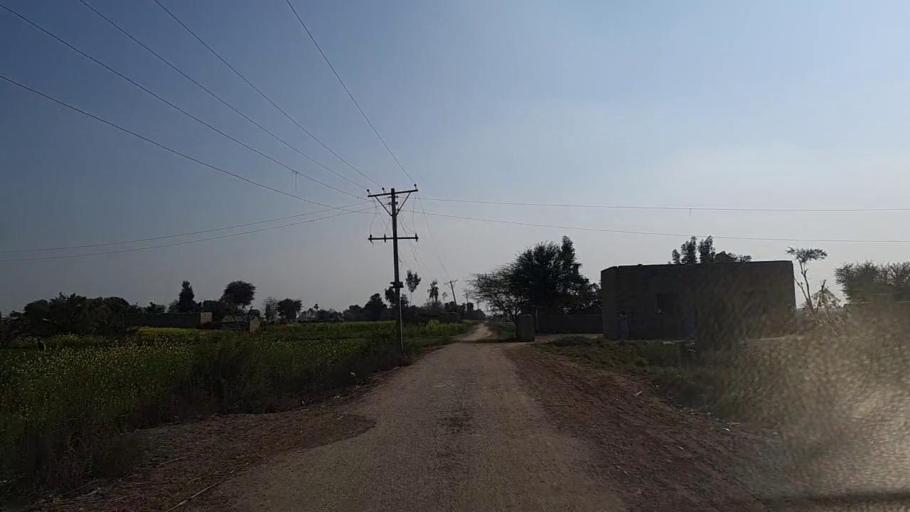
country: PK
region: Sindh
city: Jam Sahib
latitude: 26.2781
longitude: 68.6046
